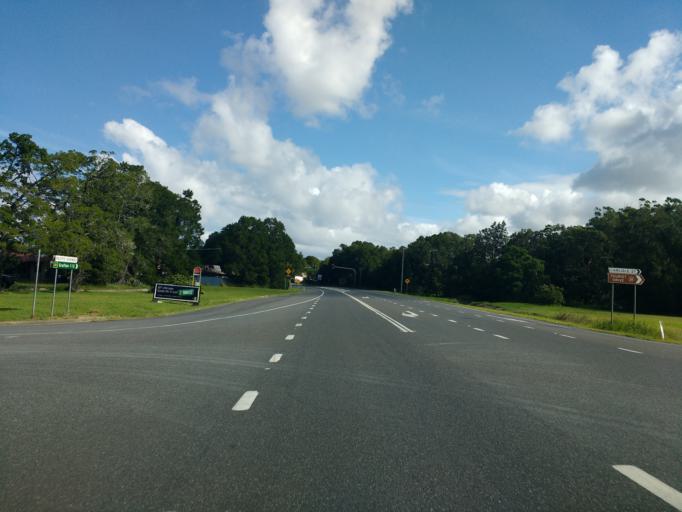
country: AU
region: New South Wales
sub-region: Ballina
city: Ballina
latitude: -28.9497
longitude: 153.4654
